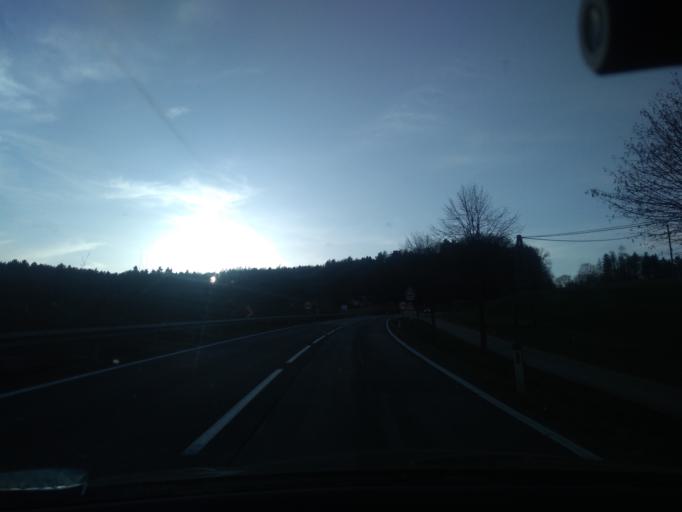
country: AT
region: Styria
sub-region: Politischer Bezirk Graz-Umgebung
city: Hausmannstatten
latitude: 46.9841
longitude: 15.5494
